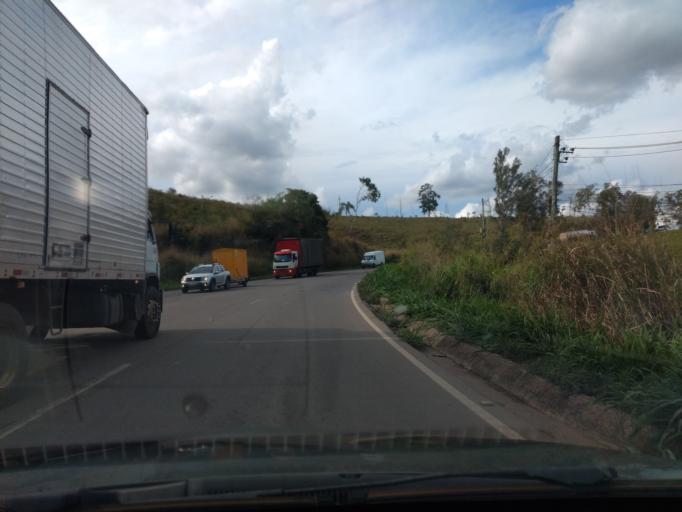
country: BR
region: Minas Gerais
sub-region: Varginha
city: Varginha
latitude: -21.6088
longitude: -45.4330
